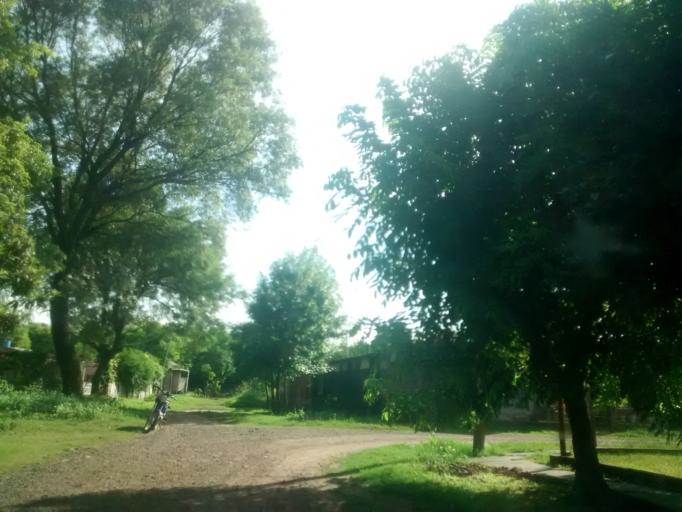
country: AR
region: Chaco
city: Puerto Tirol
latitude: -27.3684
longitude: -59.0858
